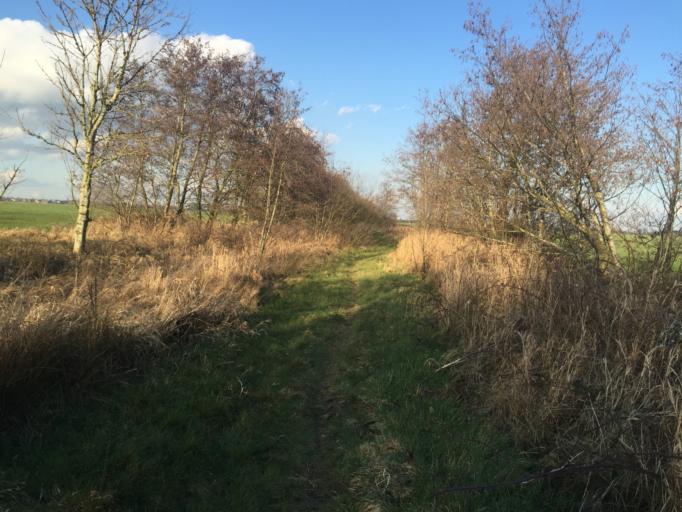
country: NL
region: Utrecht
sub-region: Gemeente Oudewater
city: Oudewater
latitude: 52.0399
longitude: 4.8205
